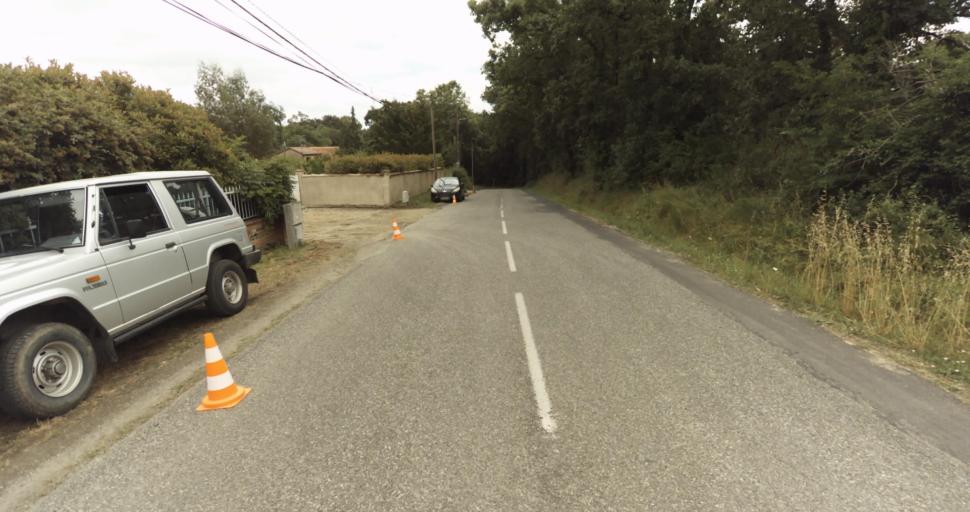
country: FR
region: Midi-Pyrenees
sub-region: Departement de la Haute-Garonne
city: Fontenilles
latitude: 43.5504
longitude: 1.1984
